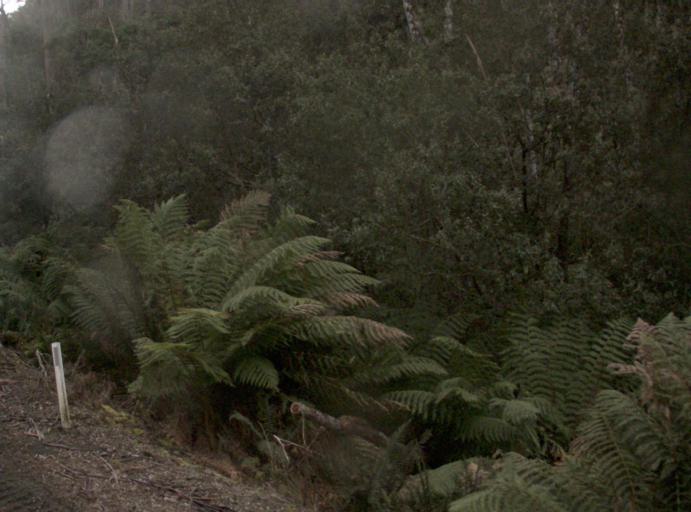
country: AU
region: Tasmania
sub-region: Dorset
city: Scottsdale
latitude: -41.3002
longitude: 147.3613
